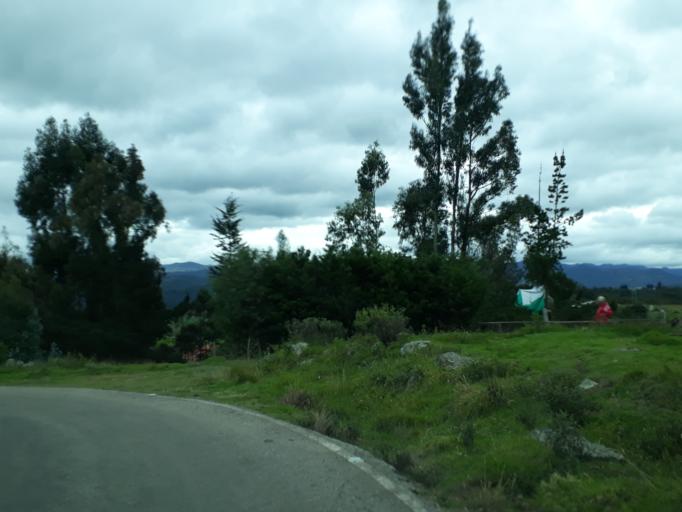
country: CO
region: Cundinamarca
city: Susa
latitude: 5.4009
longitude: -73.7760
